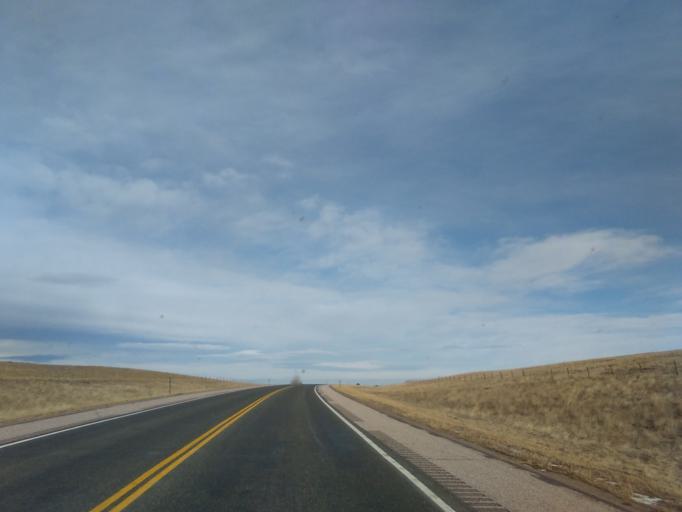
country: US
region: Wyoming
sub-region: Laramie County
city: Pine Bluffs
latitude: 41.5954
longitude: -104.2653
